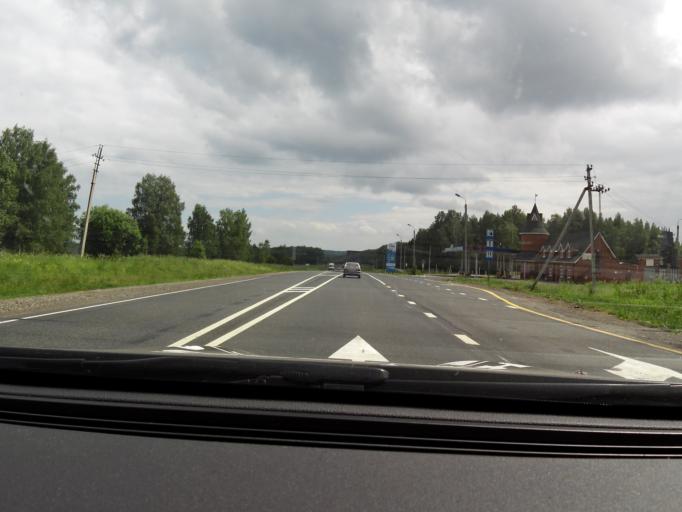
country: RU
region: Perm
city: Suksun
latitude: 57.1519
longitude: 57.2733
